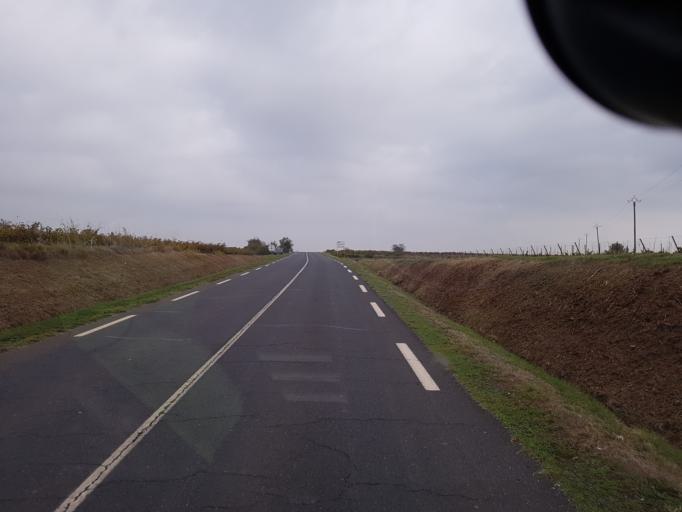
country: FR
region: Languedoc-Roussillon
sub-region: Departement de l'Herault
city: Marseillan
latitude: 43.3728
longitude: 3.5332
